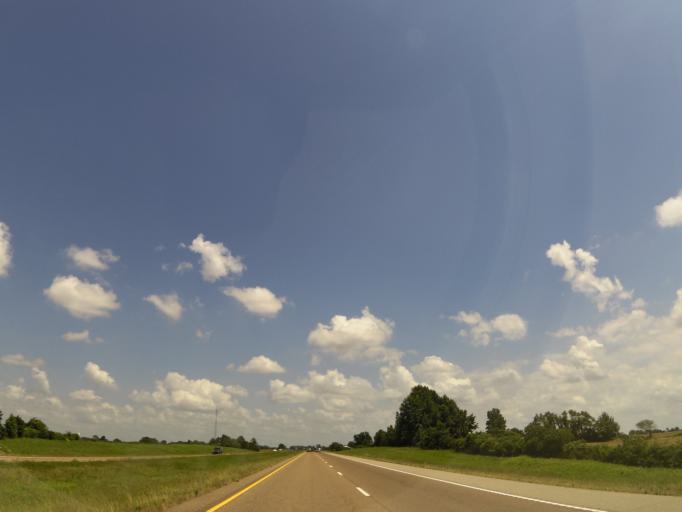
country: US
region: Tennessee
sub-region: Crockett County
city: Alamo
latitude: 35.7867
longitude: -89.1499
